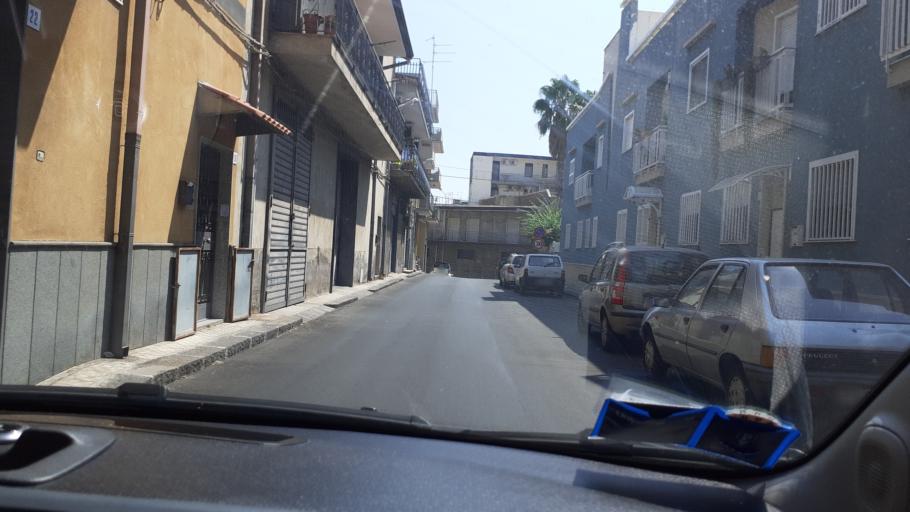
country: IT
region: Sicily
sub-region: Catania
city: Misterbianco
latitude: 37.5178
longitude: 15.0154
